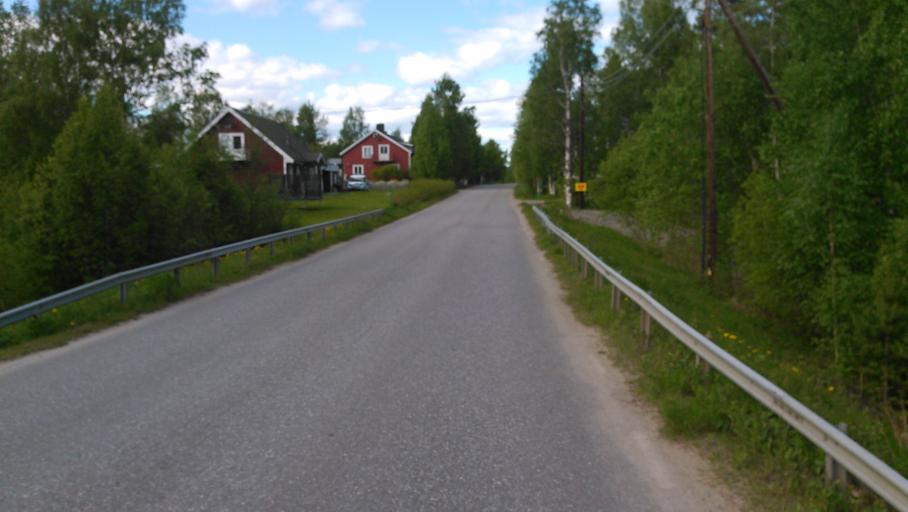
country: SE
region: Vaesterbotten
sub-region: Vannas Kommun
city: Vannasby
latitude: 63.9718
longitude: 19.8868
